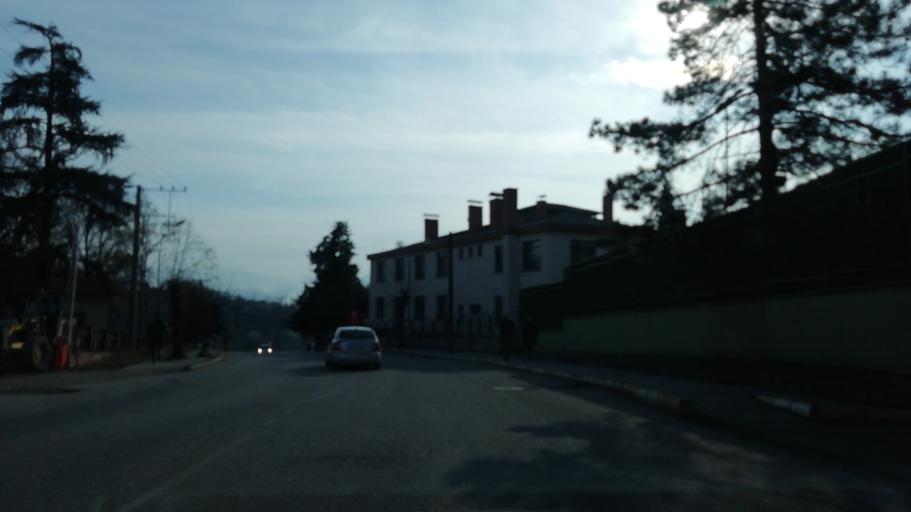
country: TR
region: Karabuk
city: Karabuk
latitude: 41.2013
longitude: 32.6264
